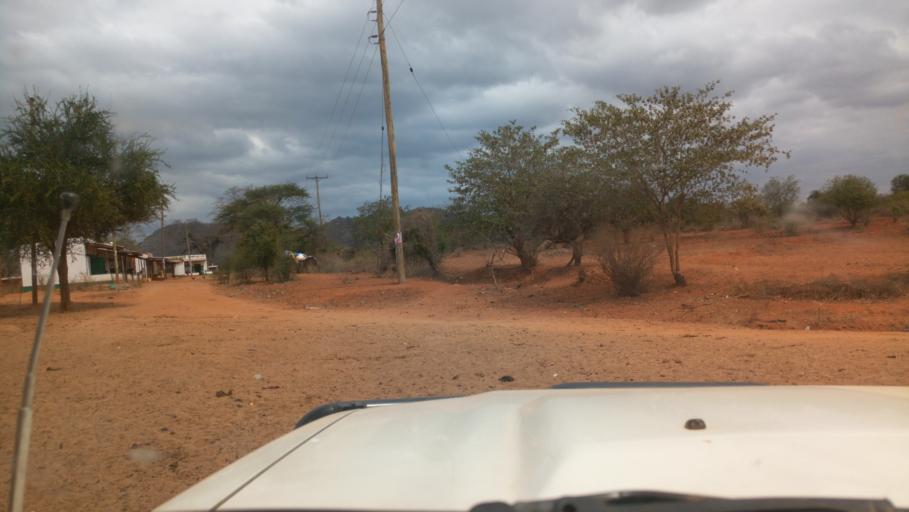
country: KE
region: Makueni
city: Mtito Andei
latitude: -2.0269
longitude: 38.3207
